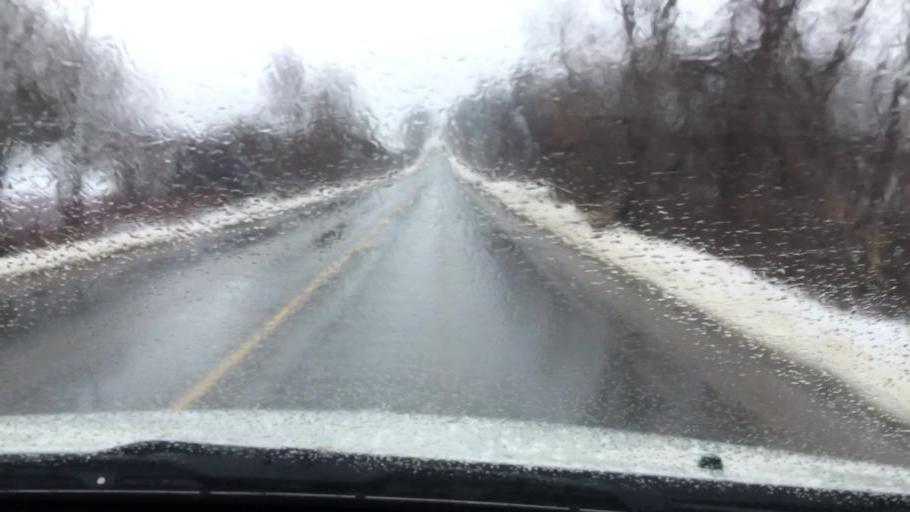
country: US
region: Michigan
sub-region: Osceola County
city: Reed City
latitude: 44.0372
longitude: -85.4438
